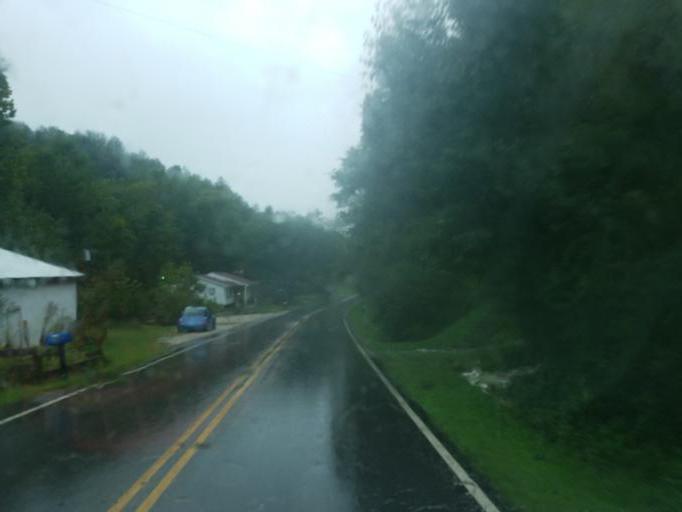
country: US
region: Kentucky
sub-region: Carter County
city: Grayson
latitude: 38.4955
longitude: -82.9967
